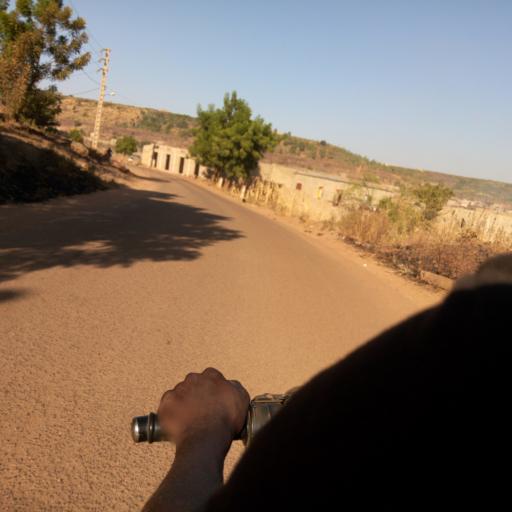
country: ML
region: Bamako
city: Bamako
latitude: 12.6584
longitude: -8.0386
